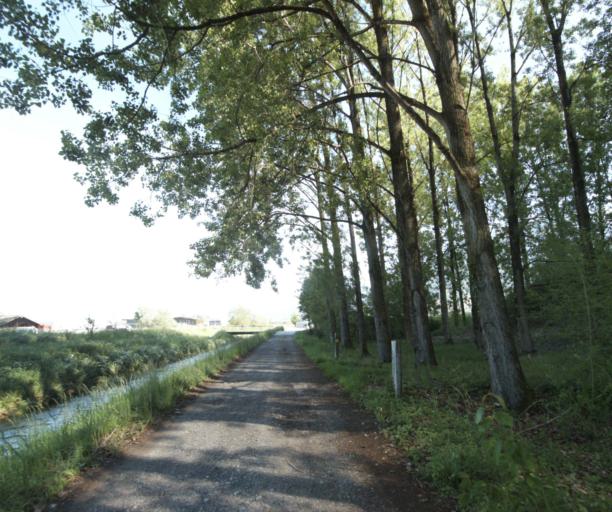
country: CH
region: Vaud
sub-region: Aigle District
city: Villeneuve
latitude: 46.3789
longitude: 6.9312
